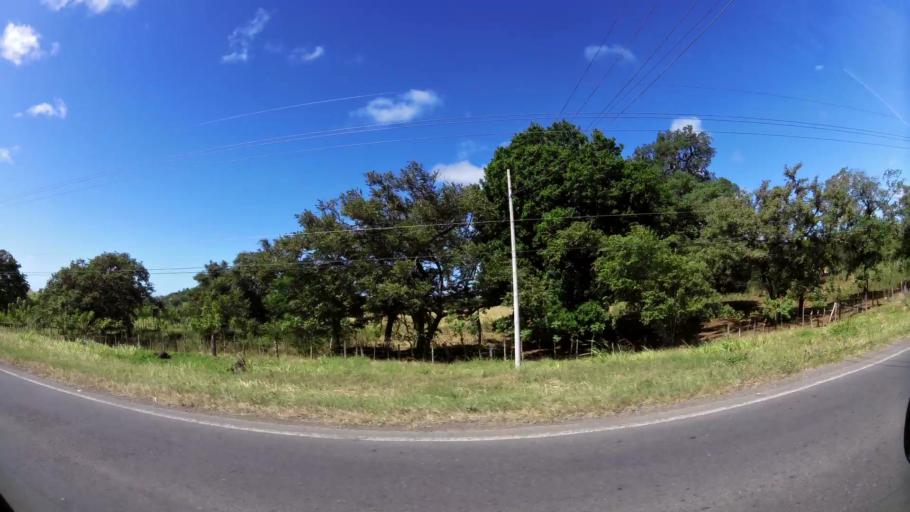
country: CR
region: Guanacaste
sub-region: Canton de Canas
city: Canas
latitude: 10.4068
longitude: -85.0862
